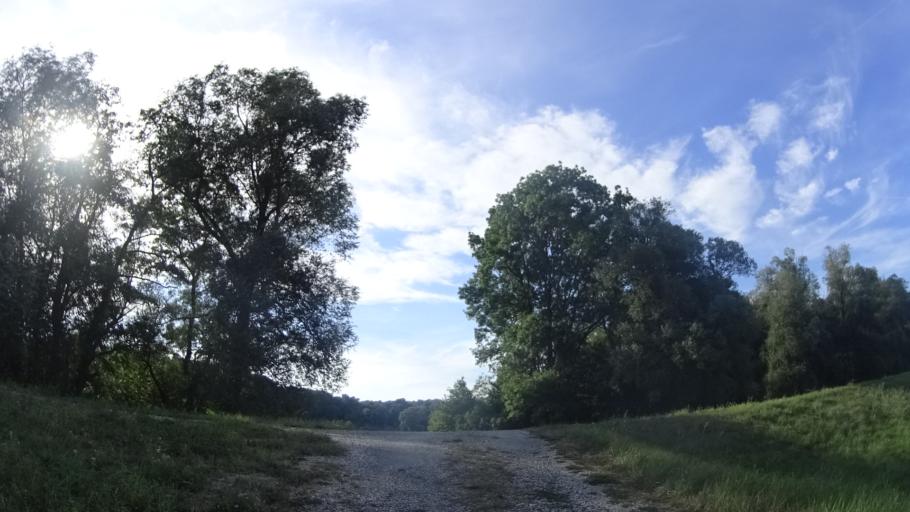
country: AT
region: Lower Austria
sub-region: Politischer Bezirk Mistelbach
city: Rabensburg
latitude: 48.6075
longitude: 16.9470
